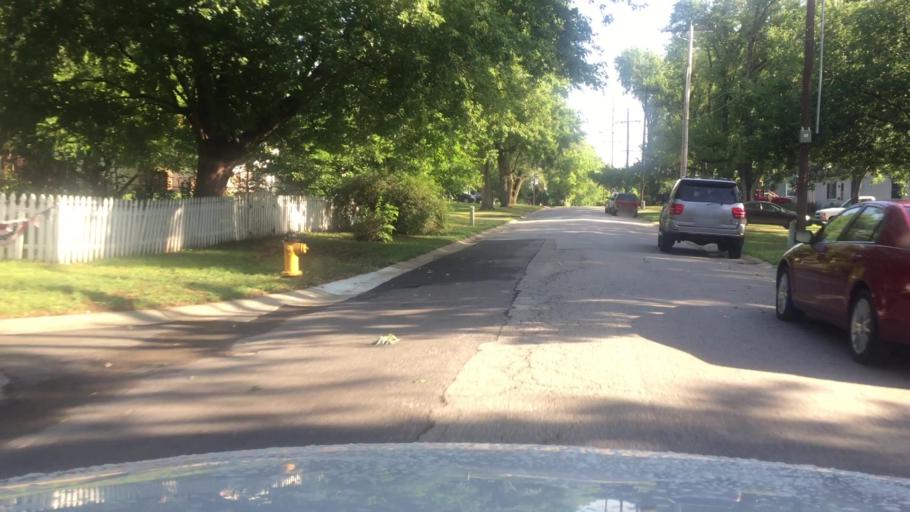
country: US
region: Kansas
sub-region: Johnson County
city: Shawnee
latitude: 39.0351
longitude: -94.7285
